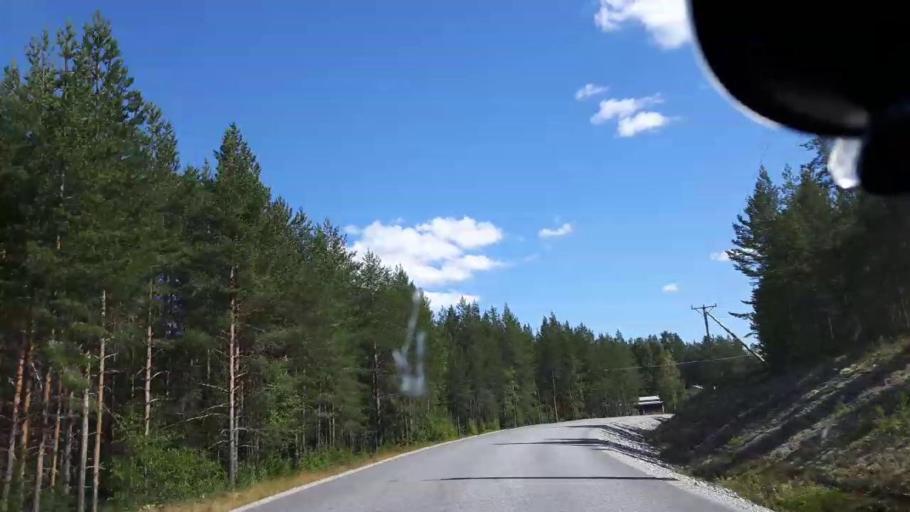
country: SE
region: Vaesternorrland
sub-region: Ange Kommun
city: Fransta
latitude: 62.7006
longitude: 16.3870
